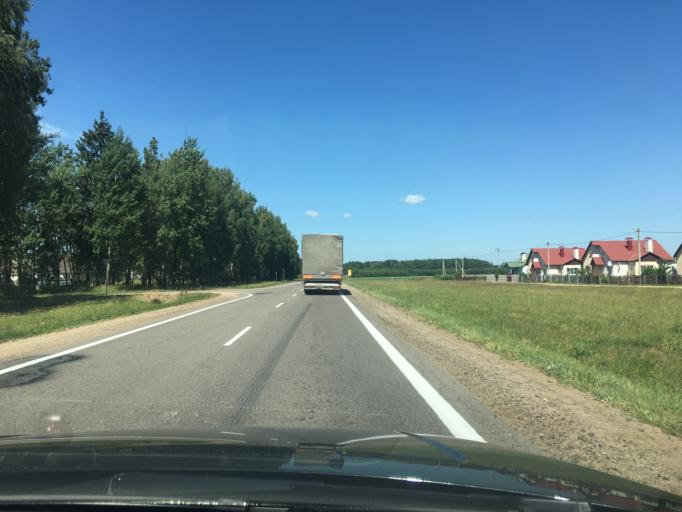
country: BY
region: Grodnenskaya
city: Iwye
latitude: 54.0375
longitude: 25.9202
